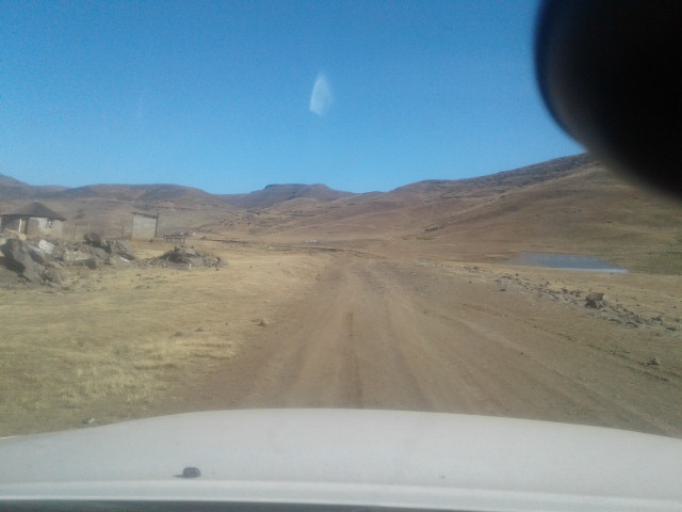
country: LS
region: Berea
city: Teyateyaneng
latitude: -29.3707
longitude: 28.0267
